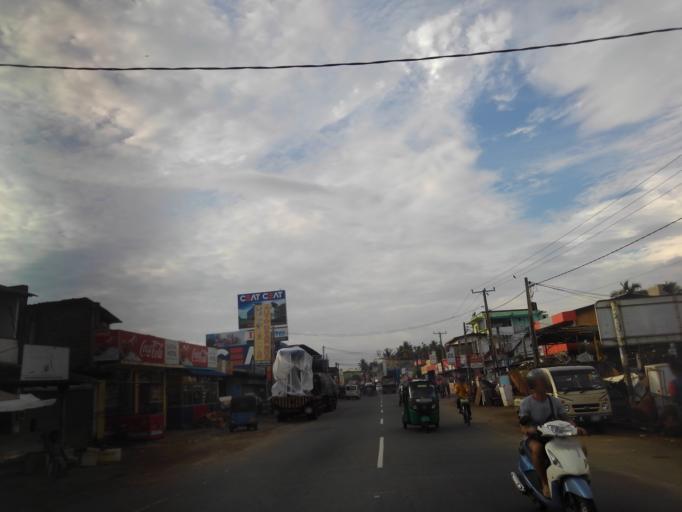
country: LK
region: Southern
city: Unawatuna
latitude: 6.0309
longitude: 80.2408
